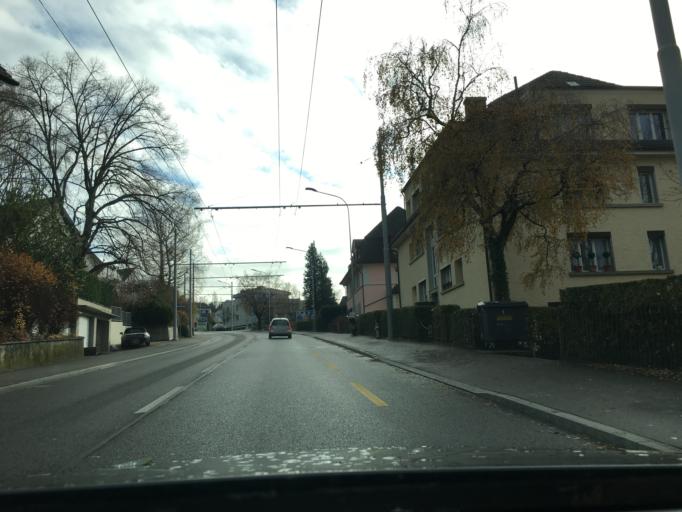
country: CH
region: Zurich
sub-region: Bezirk Zuerich
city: Zuerich (Kreis 7) / Witikon
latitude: 47.3589
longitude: 8.5824
